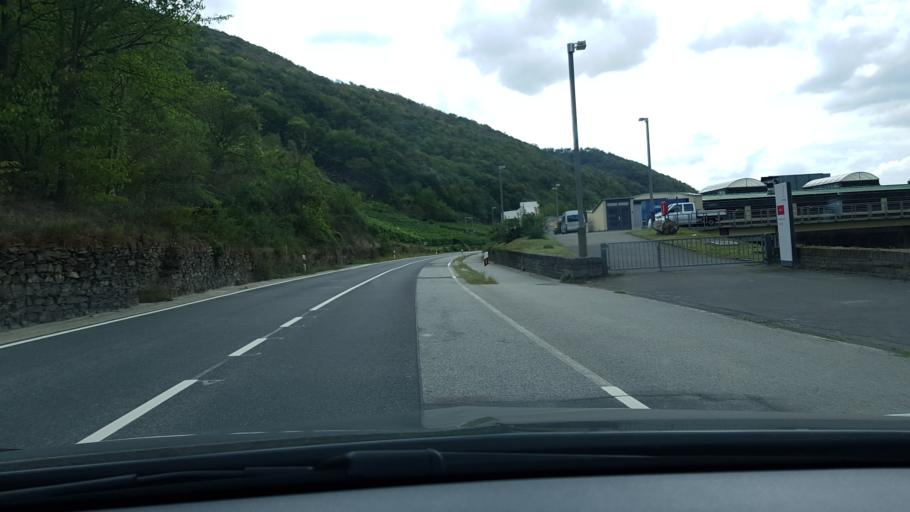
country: DE
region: Rheinland-Pfalz
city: Niederfell
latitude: 50.2756
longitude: 7.4609
